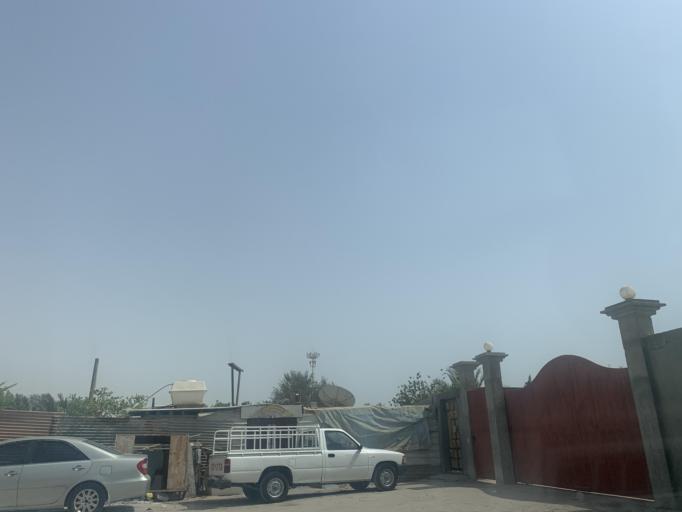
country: BH
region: Manama
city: Jidd Hafs
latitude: 26.2125
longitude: 50.4638
